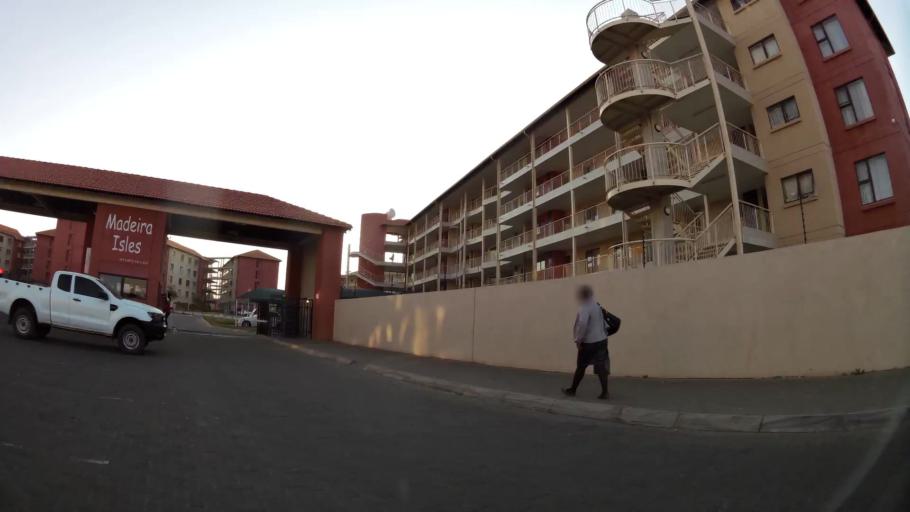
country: ZA
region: Gauteng
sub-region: City of Tshwane Metropolitan Municipality
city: Pretoria
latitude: -25.7481
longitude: 28.1134
